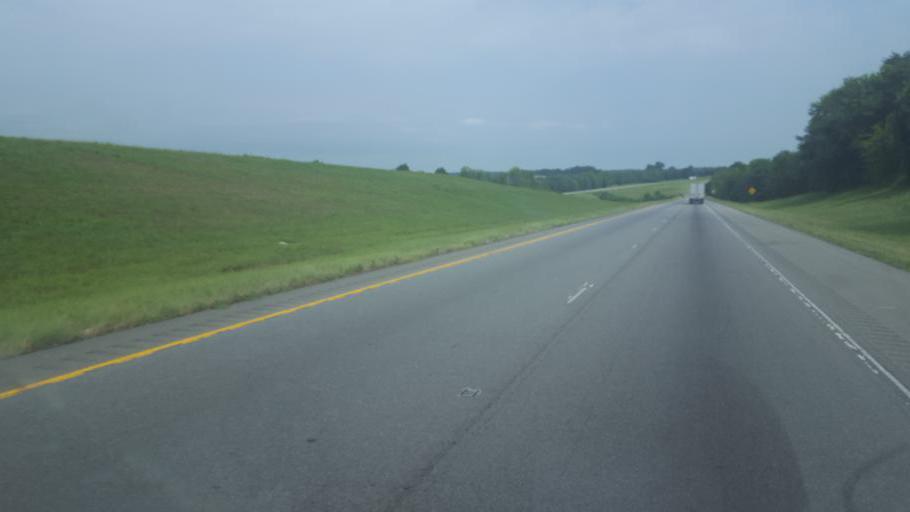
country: US
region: North Carolina
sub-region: Iredell County
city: Statesville
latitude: 35.9243
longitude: -80.8549
